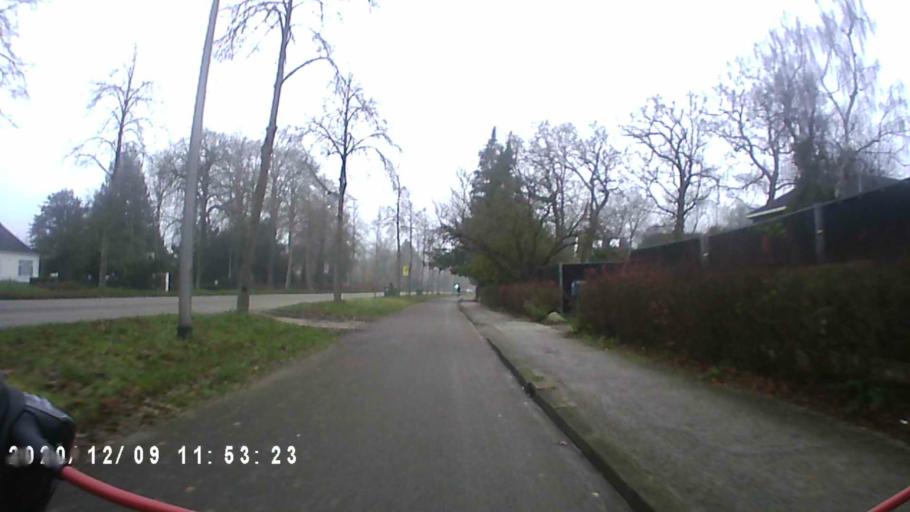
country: NL
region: Groningen
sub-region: Gemeente Haren
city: Haren
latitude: 53.1796
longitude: 6.5961
